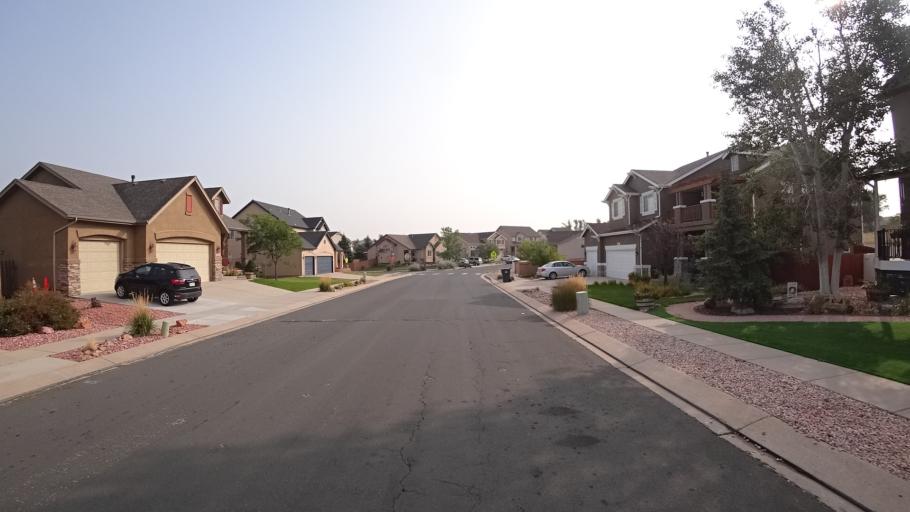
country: US
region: Colorado
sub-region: El Paso County
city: Cimarron Hills
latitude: 38.9342
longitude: -104.7342
